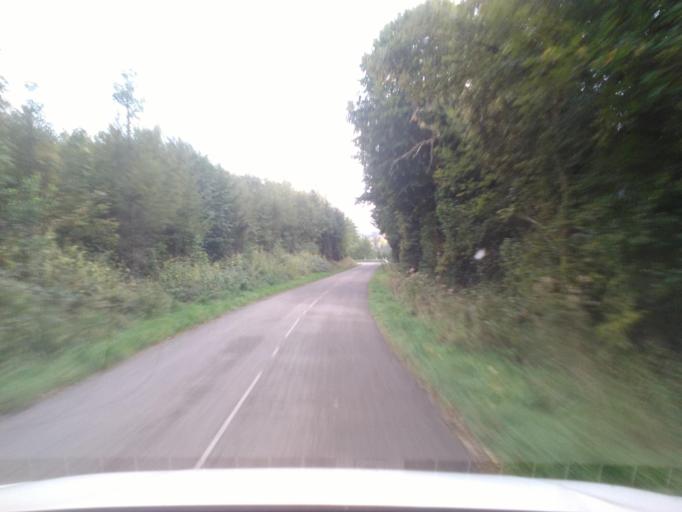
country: FR
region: Lorraine
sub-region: Departement des Vosges
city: Senones
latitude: 48.3955
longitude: 7.0236
